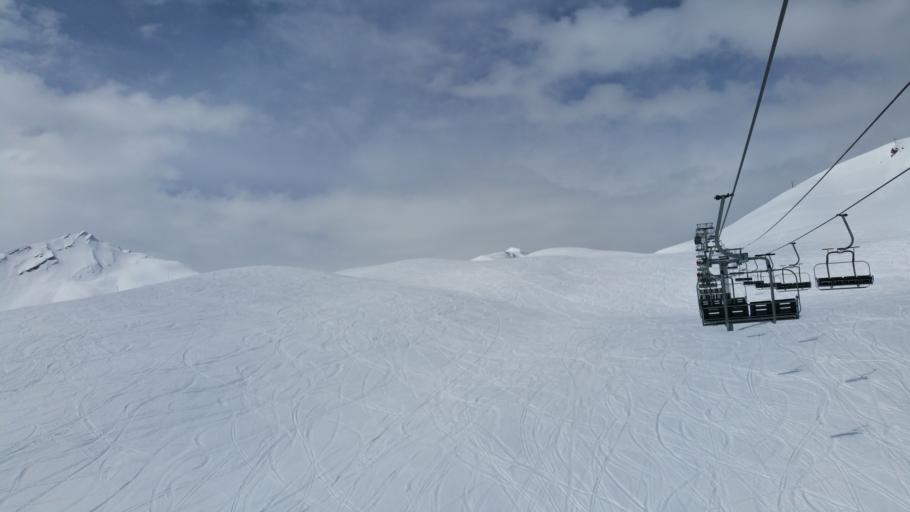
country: FR
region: Rhone-Alpes
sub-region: Departement de la Savoie
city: Valloire
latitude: 45.1998
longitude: 6.3931
